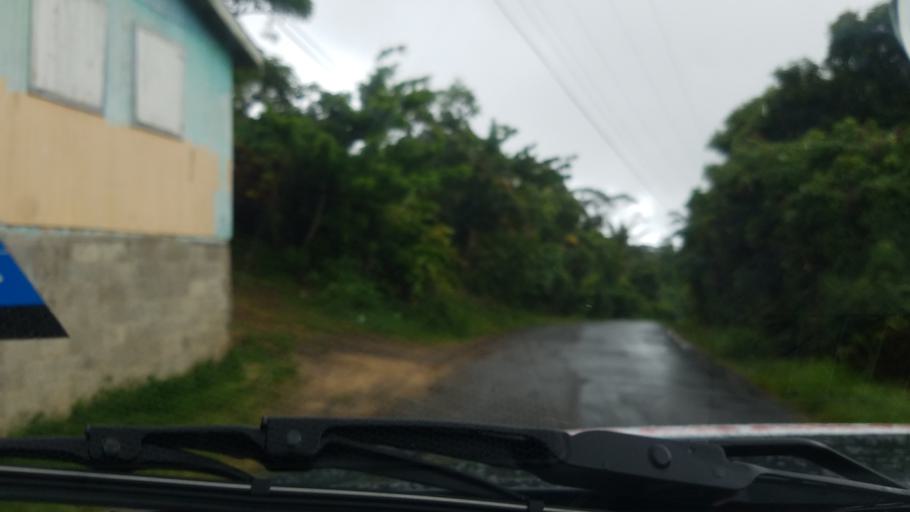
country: LC
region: Castries Quarter
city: Bisee
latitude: 14.0213
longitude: -60.9347
